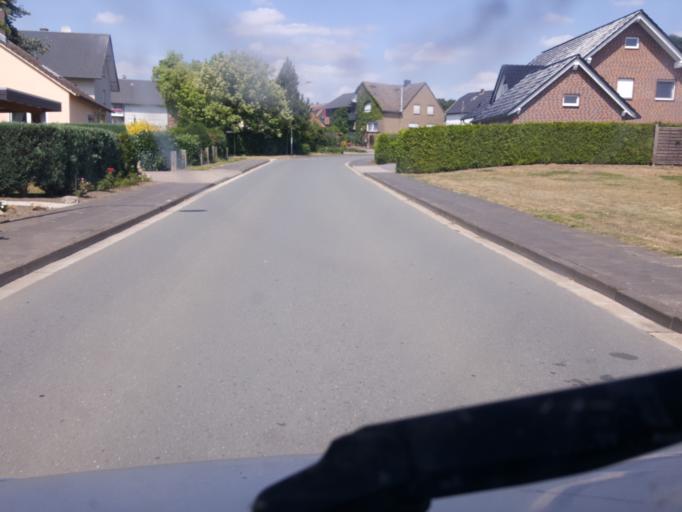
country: DE
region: North Rhine-Westphalia
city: Bad Oeynhausen
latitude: 52.2192
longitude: 8.7617
